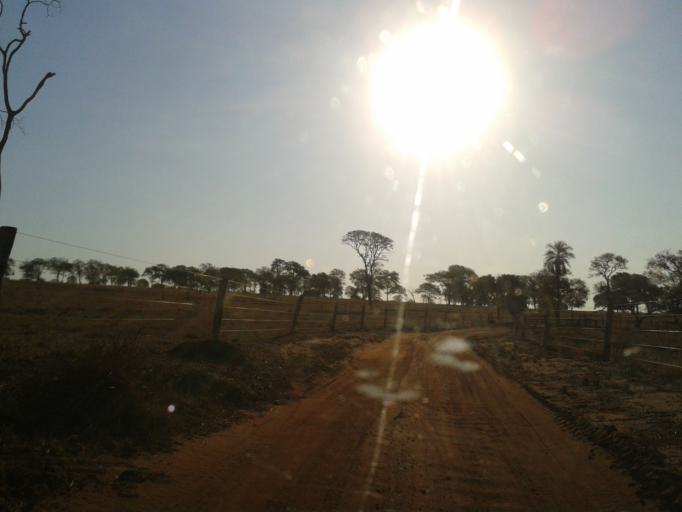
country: BR
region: Minas Gerais
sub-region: Ituiutaba
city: Ituiutaba
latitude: -19.2483
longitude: -49.5830
